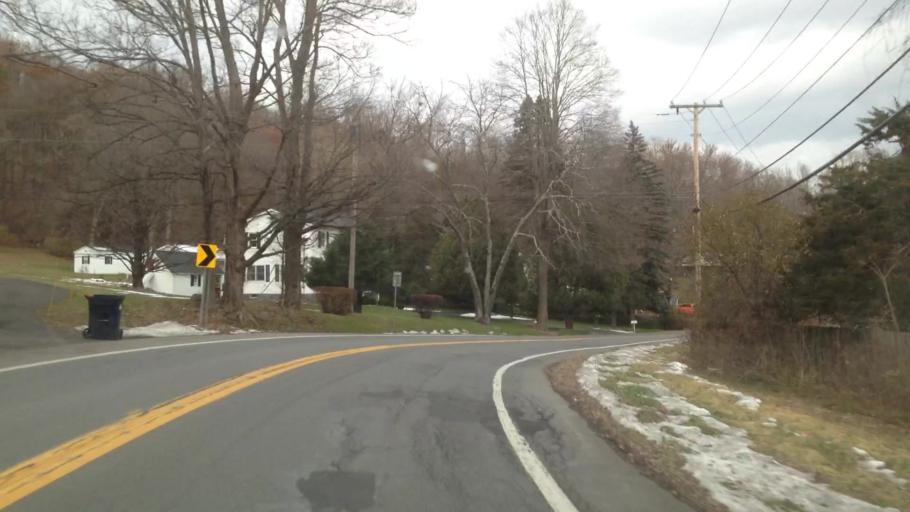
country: US
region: New York
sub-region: Ulster County
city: Lake Katrine
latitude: 41.9967
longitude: -73.9711
